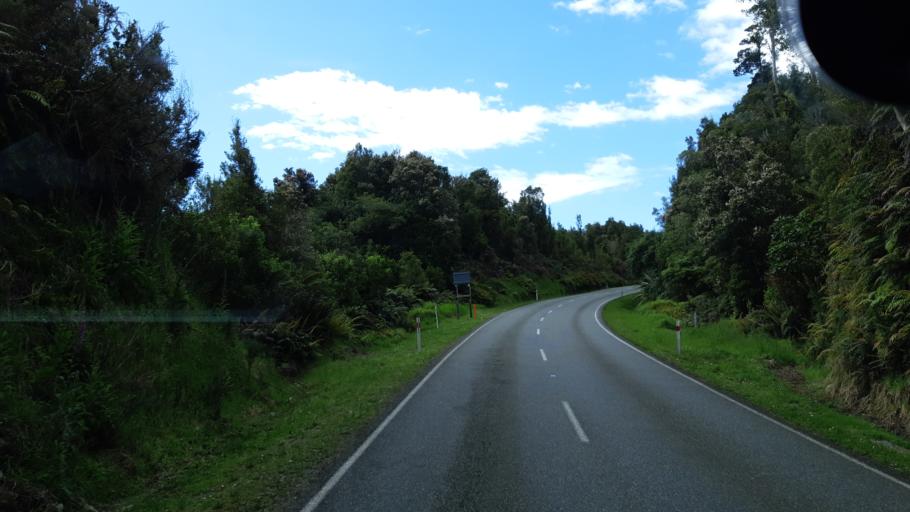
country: NZ
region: West Coast
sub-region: Westland District
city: Hokitika
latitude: -43.0479
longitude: 170.6379
